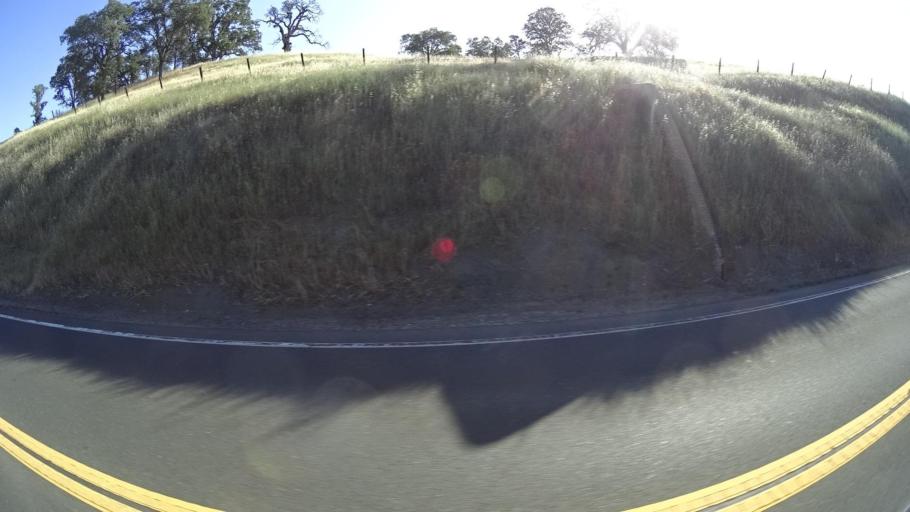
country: US
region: California
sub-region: Lake County
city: Upper Lake
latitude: 39.1418
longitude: -122.9137
